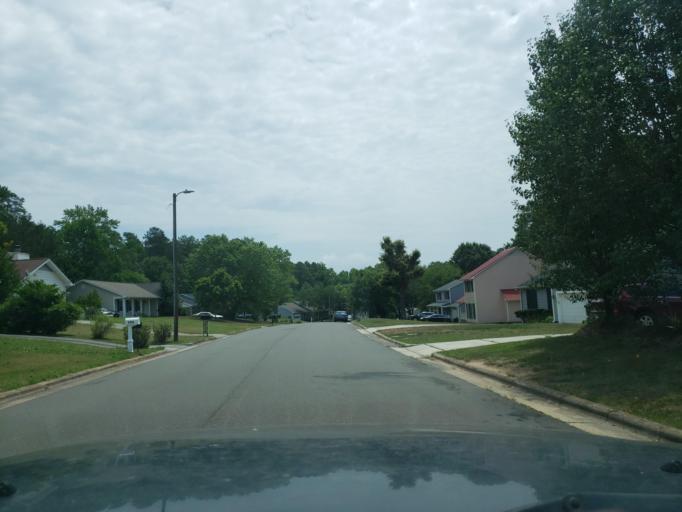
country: US
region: North Carolina
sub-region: Durham County
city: Durham
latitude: 35.9544
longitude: -78.9316
